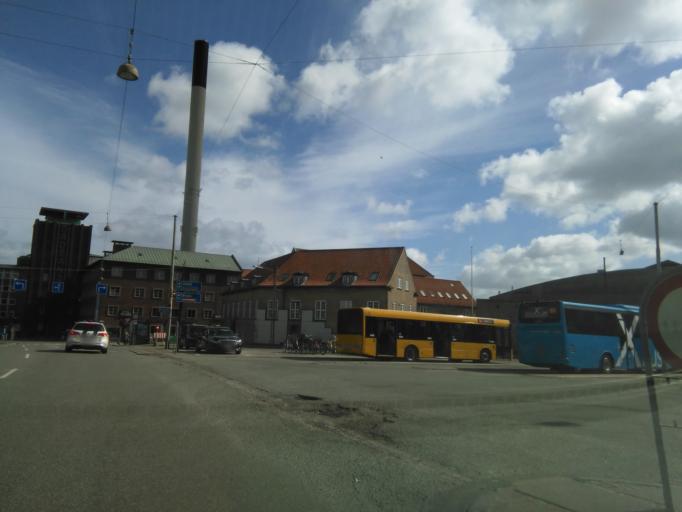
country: DK
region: Central Jutland
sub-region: Arhus Kommune
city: Arhus
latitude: 56.1522
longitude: 10.2095
